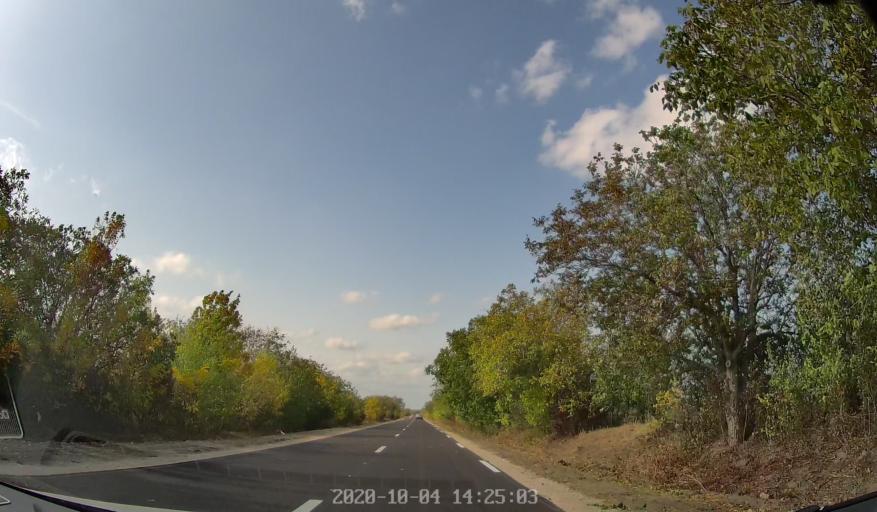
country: MD
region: Rezina
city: Saharna
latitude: 47.6176
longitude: 28.9054
